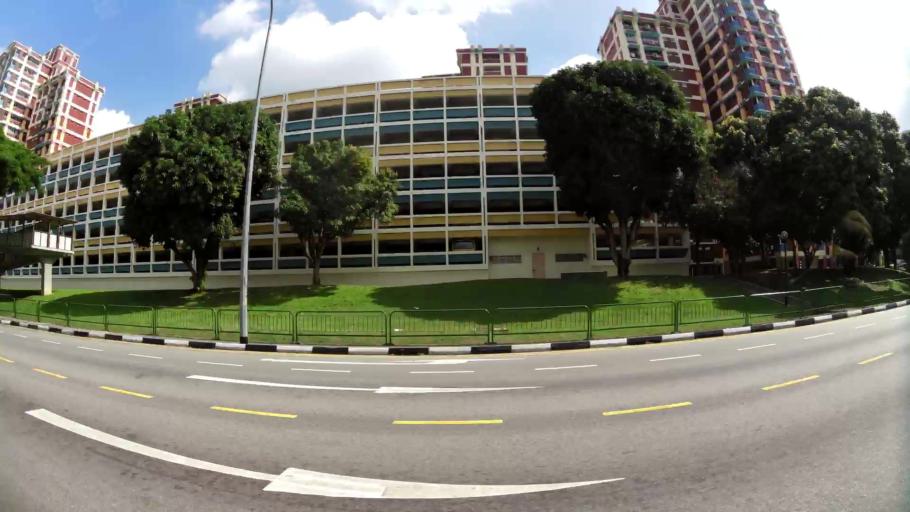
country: SG
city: Singapore
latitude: 1.3301
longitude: 103.9043
